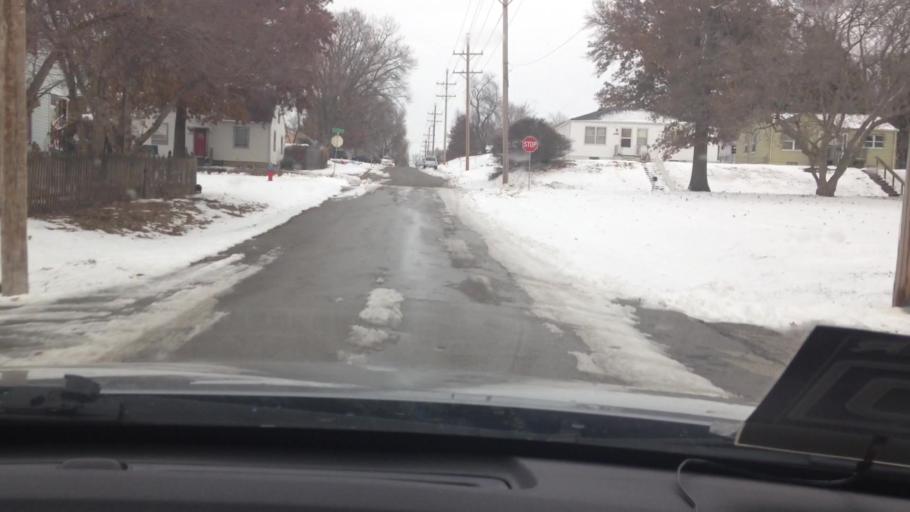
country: US
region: Kansas
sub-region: Leavenworth County
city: Leavenworth
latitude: 39.3258
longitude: -94.9333
